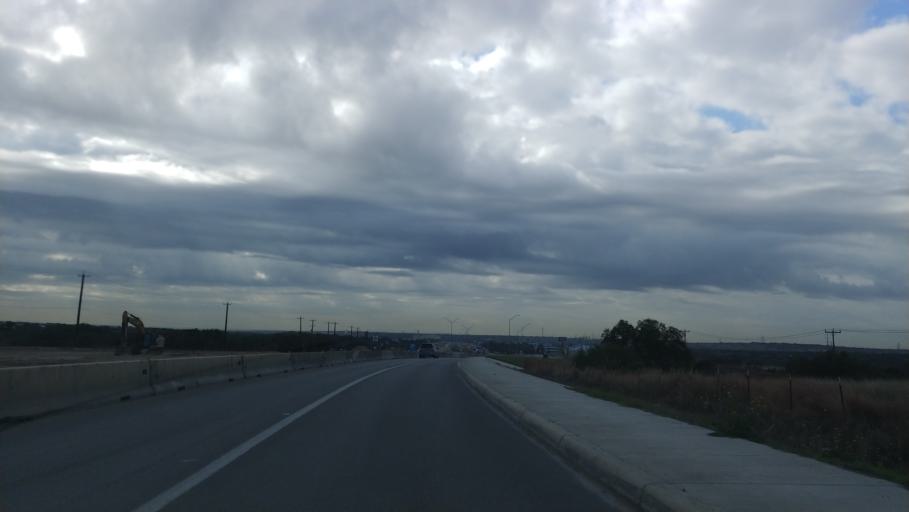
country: US
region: Texas
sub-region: Bexar County
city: Leon Valley
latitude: 29.4558
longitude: -98.7114
